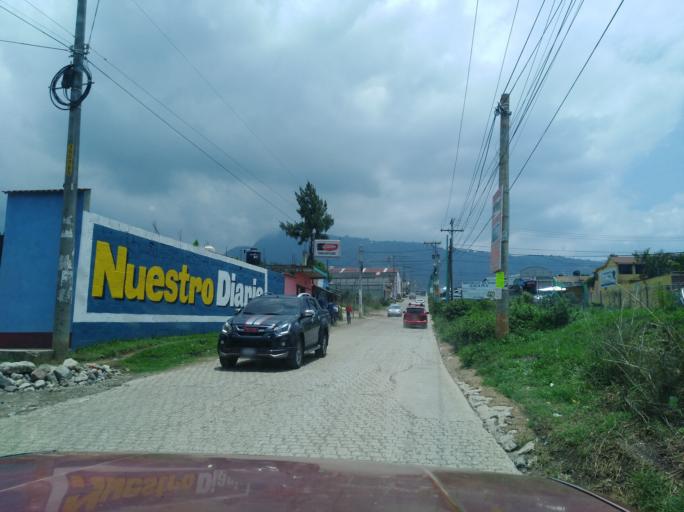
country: GT
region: Guatemala
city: Villa Nueva
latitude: 14.5276
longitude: -90.6187
